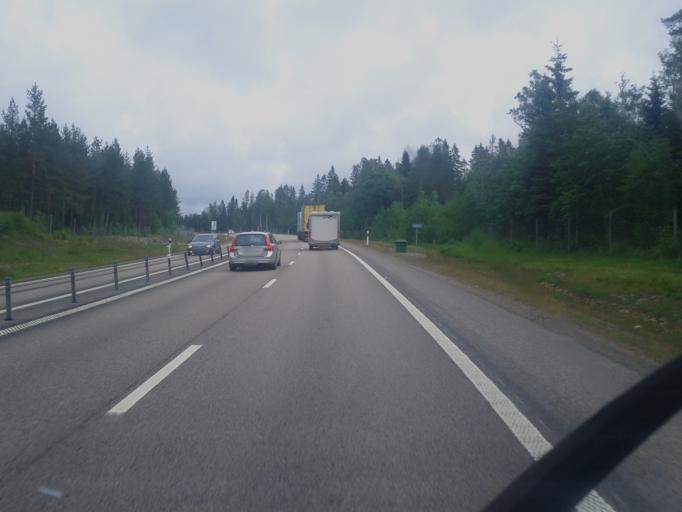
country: SE
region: Vaesternorrland
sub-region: Haernoesands Kommun
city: Haernoesand
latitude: 62.5634
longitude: 17.7264
